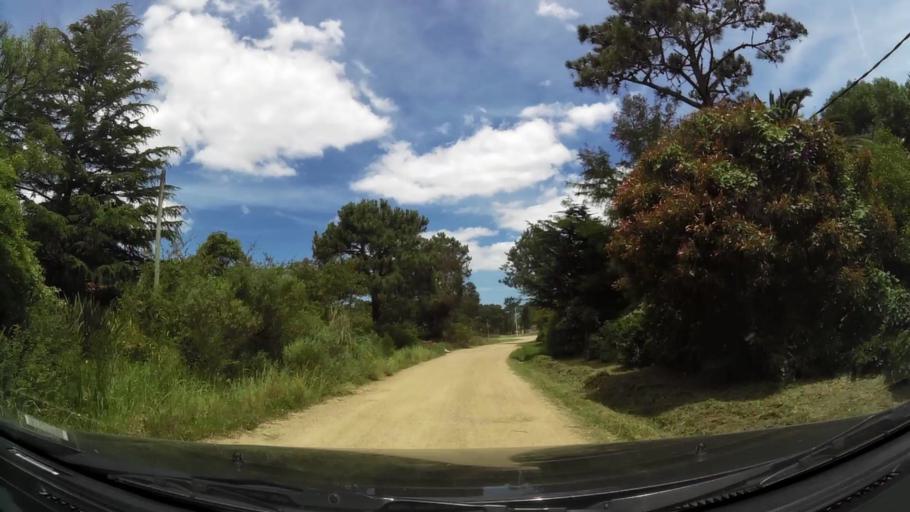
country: UY
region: Canelones
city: Pando
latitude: -34.8001
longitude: -55.8948
